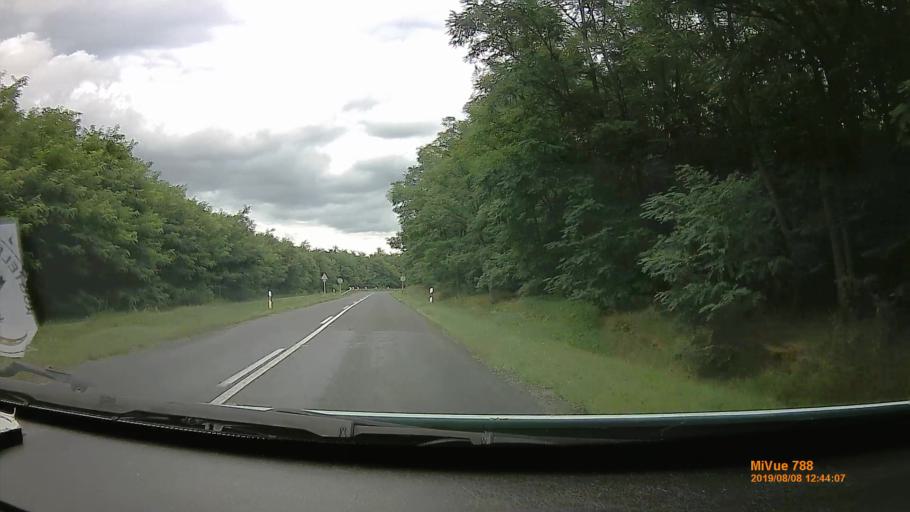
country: HU
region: Szabolcs-Szatmar-Bereg
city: Hodasz
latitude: 47.8814
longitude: 22.1934
